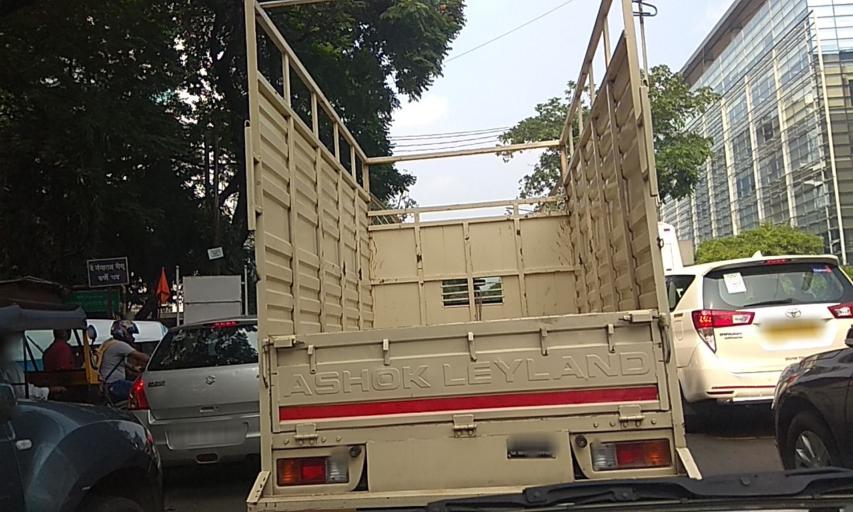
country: IN
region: Maharashtra
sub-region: Pune Division
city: Khadki
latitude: 18.5526
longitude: 73.8929
